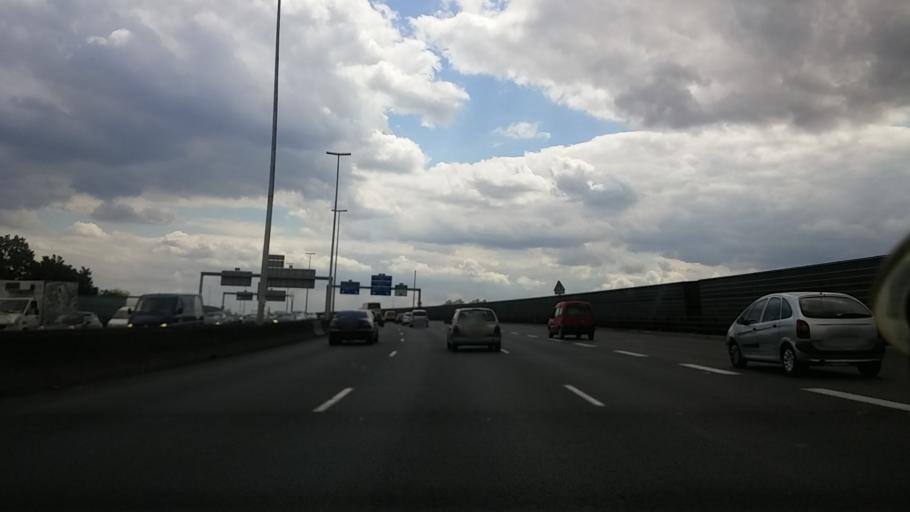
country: FR
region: Ile-de-France
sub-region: Departement de Seine-Saint-Denis
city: Noisy-le-Sec
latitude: 48.8984
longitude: 2.4695
